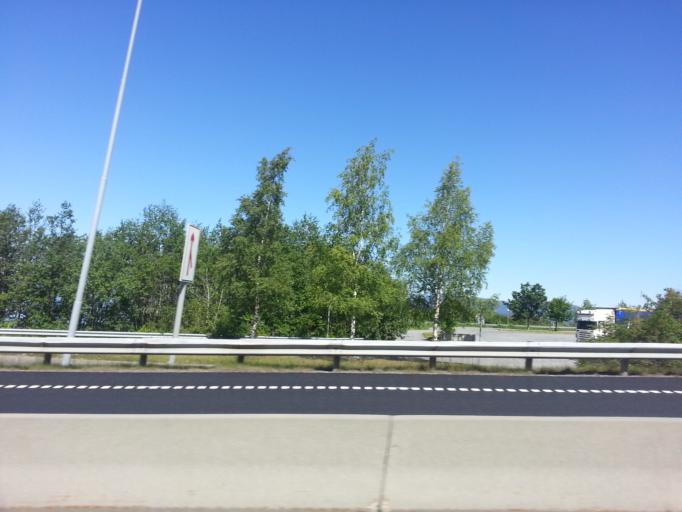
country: NO
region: Sor-Trondelag
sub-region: Malvik
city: Malvik
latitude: 63.4245
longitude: 10.7267
